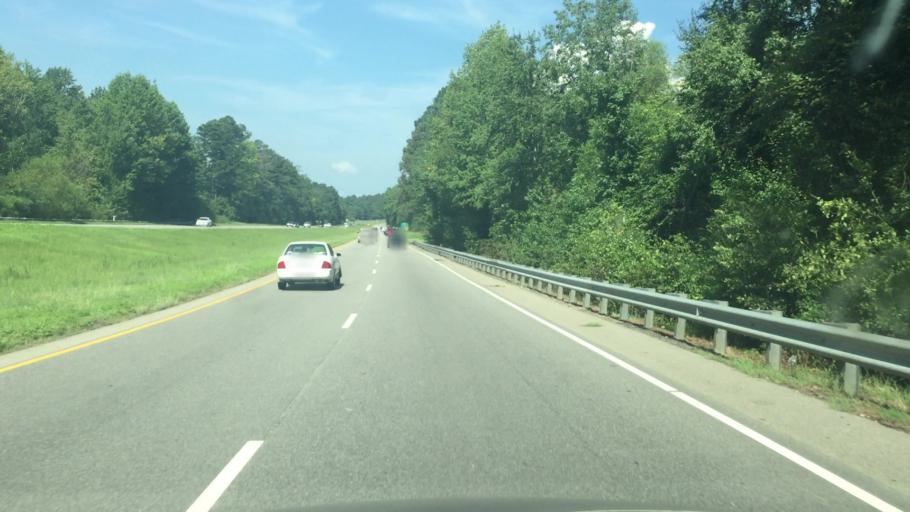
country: US
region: North Carolina
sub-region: Scotland County
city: Laurel Hill
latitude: 34.7992
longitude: -79.5230
